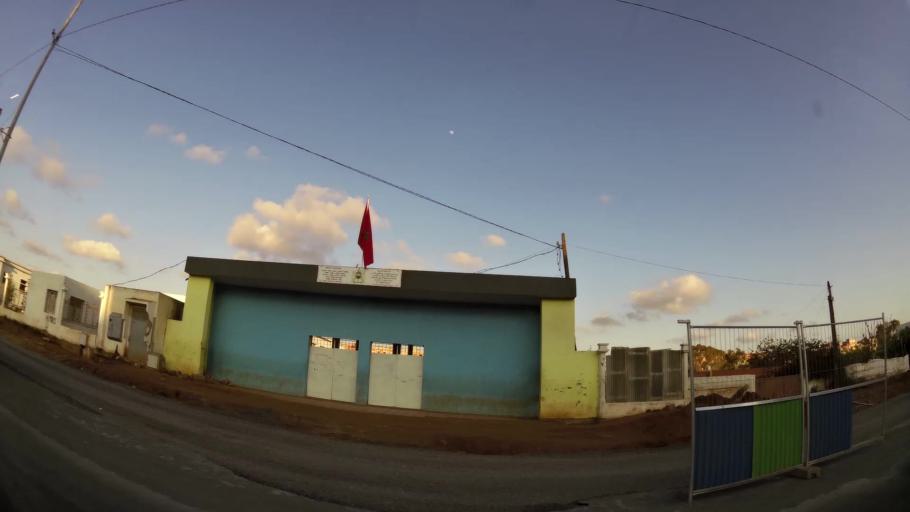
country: MA
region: Rabat-Sale-Zemmour-Zaer
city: Sale
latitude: 34.1265
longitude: -6.7363
